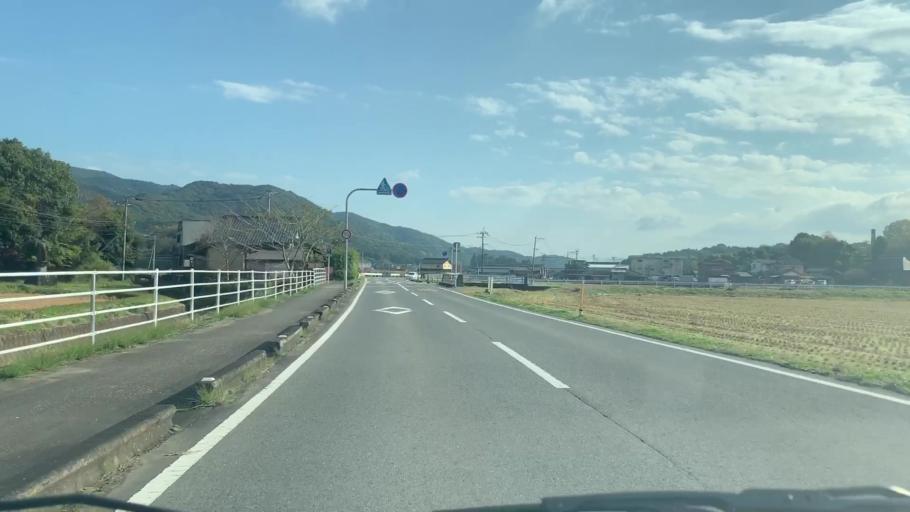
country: JP
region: Saga Prefecture
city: Takeocho-takeo
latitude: 33.1601
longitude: 130.0616
